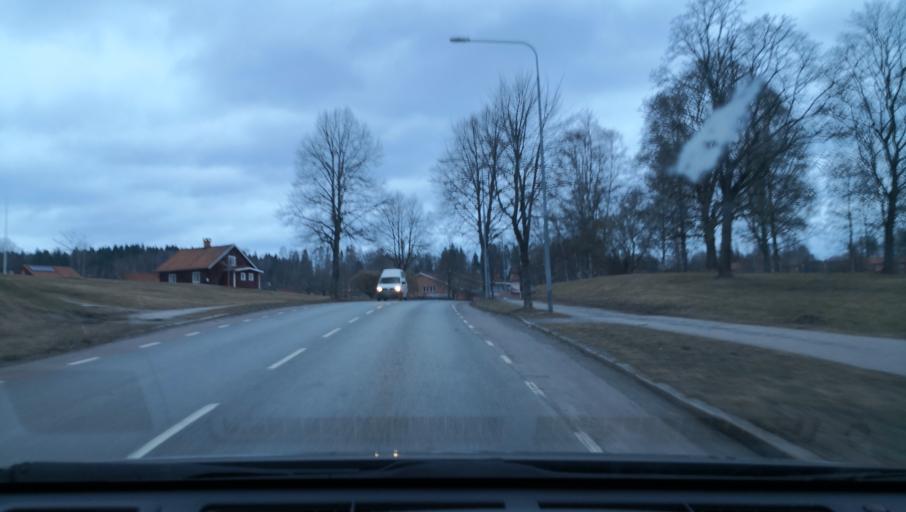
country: SE
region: Vaestmanland
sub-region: Kopings Kommun
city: Kolsva
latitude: 59.5986
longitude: 15.8373
